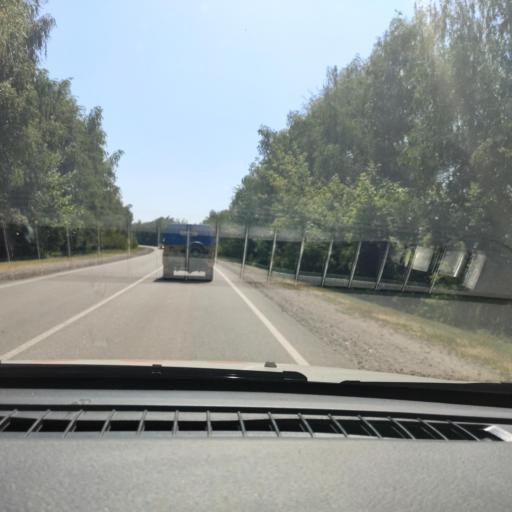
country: RU
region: Voronezj
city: Imeni Pervogo Maya
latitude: 50.7326
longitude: 39.3924
